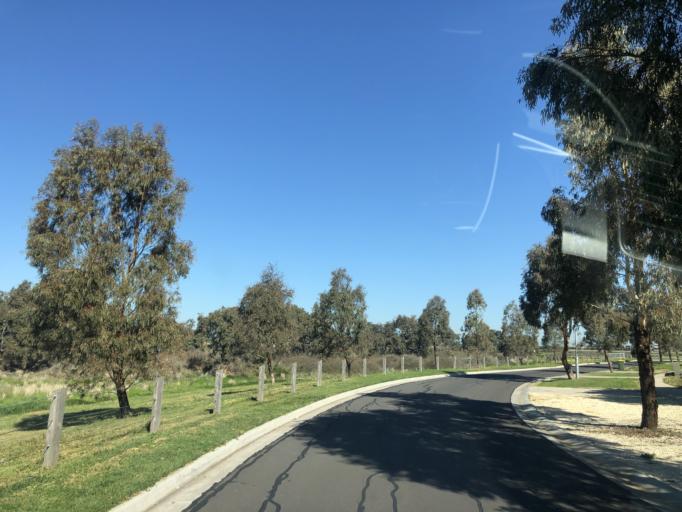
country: AU
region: Victoria
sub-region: Wyndham
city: Point Cook
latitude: -37.9111
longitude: 144.7296
